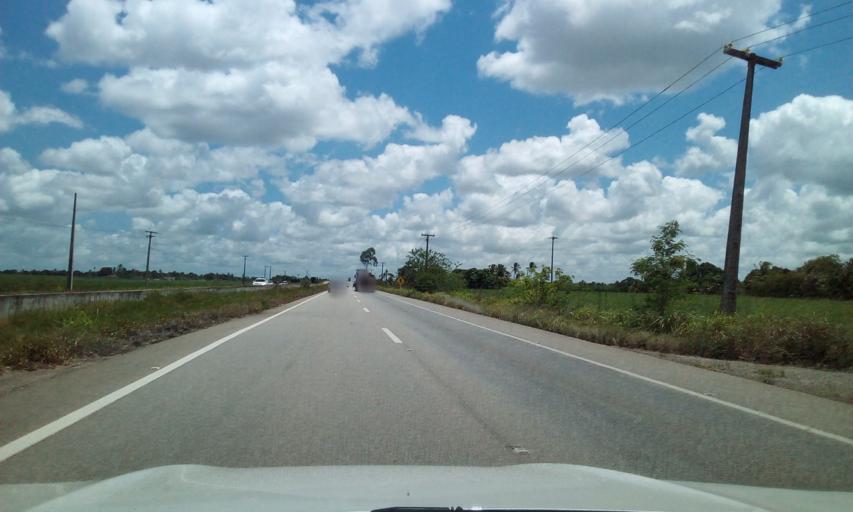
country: BR
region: Alagoas
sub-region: Junqueiro
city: Junqueiro
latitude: -9.8876
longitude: -36.3860
